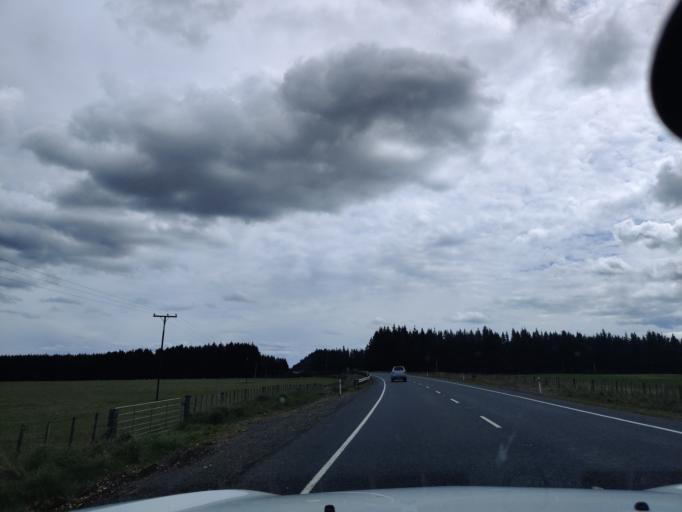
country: NZ
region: Manawatu-Wanganui
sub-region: Ruapehu District
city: Waiouru
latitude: -39.4672
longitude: 175.5824
